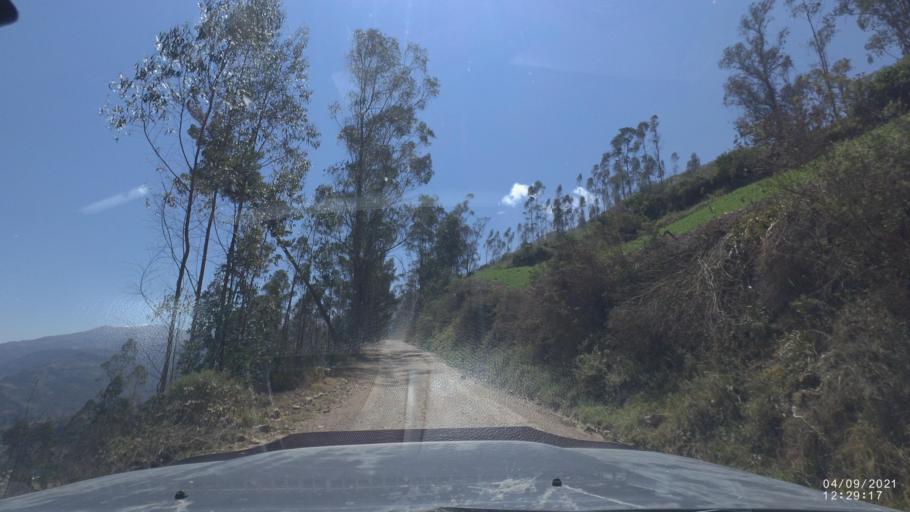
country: BO
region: Cochabamba
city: Colchani
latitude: -17.2246
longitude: -66.5253
